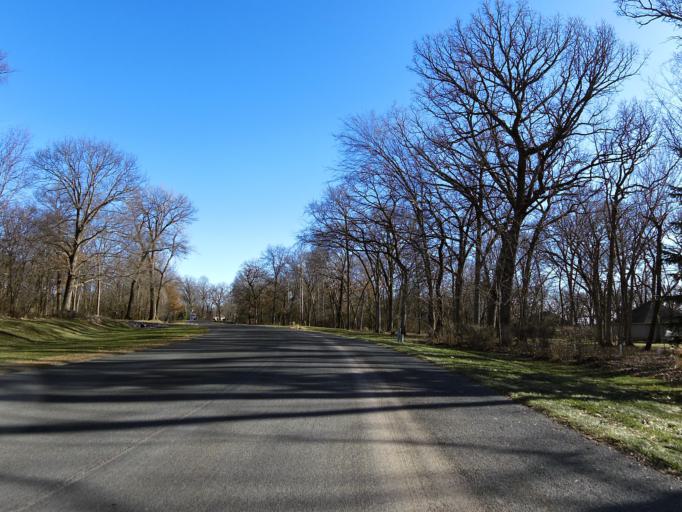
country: US
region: Minnesota
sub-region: Washington County
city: Bayport
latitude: 44.9847
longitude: -92.8035
